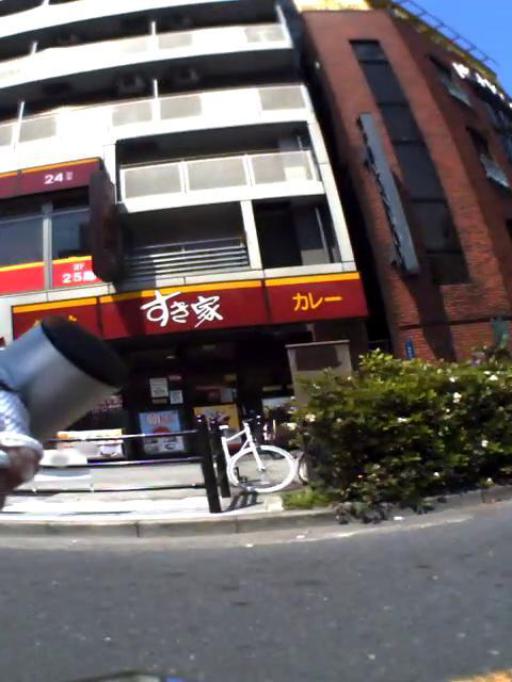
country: JP
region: Osaka
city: Osaka-shi
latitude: 34.6833
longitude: 135.5173
